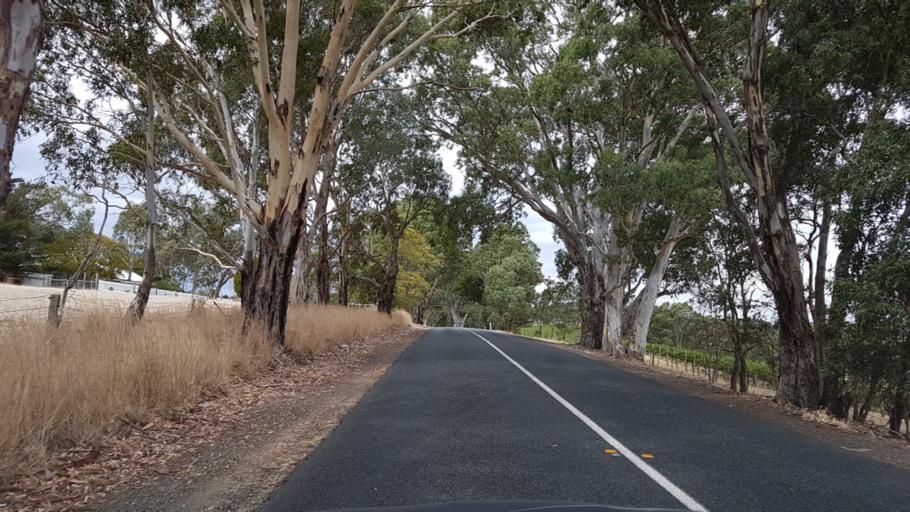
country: AU
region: South Australia
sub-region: Adelaide Hills
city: Gumeracha
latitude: -34.7824
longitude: 138.9176
